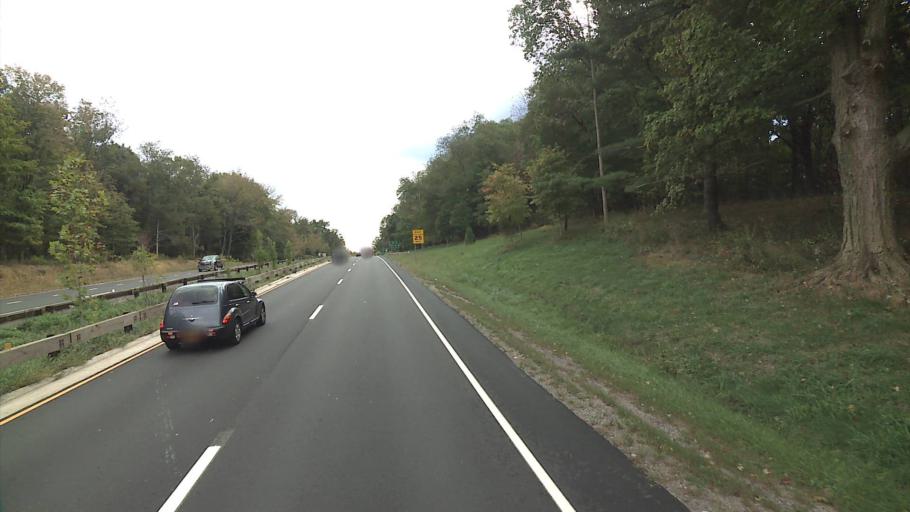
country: US
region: Connecticut
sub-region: Fairfield County
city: North Stamford
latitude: 41.1007
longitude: -73.5797
